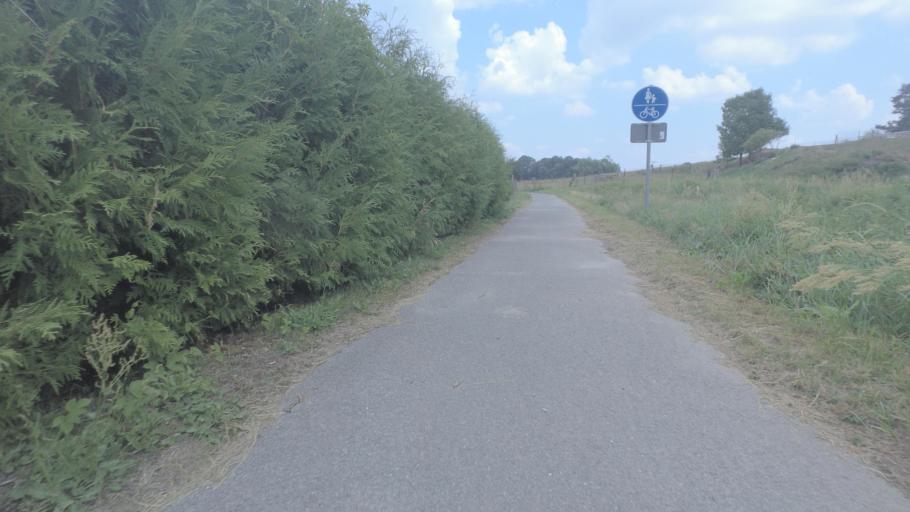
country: DE
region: Mecklenburg-Vorpommern
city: Borrentin
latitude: 53.8502
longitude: 12.9605
